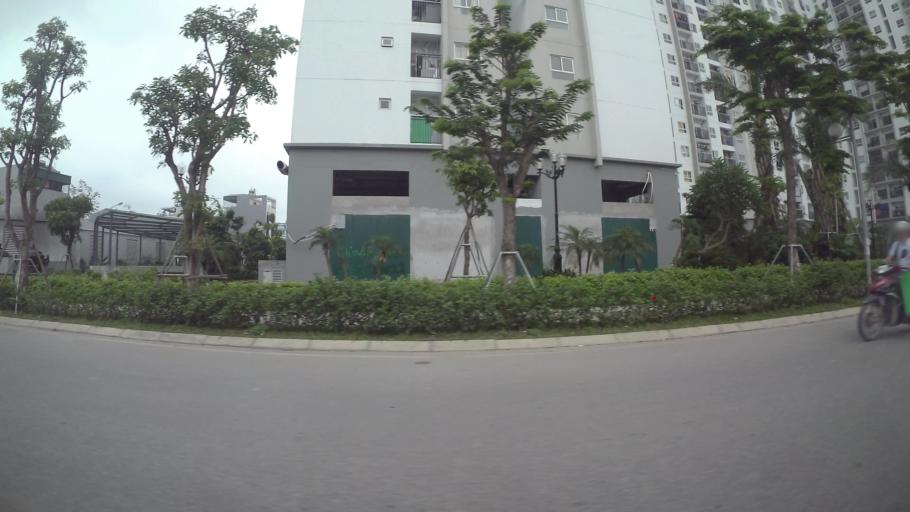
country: VN
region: Ha Noi
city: Trau Quy
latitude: 21.0407
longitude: 105.9271
